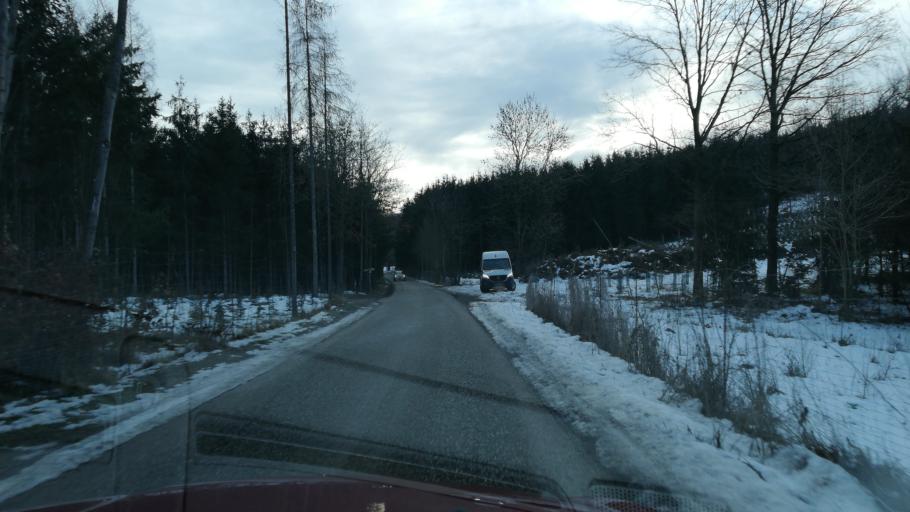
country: AT
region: Upper Austria
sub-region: Wels-Land
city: Buchkirchen
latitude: 48.2388
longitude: 13.9854
